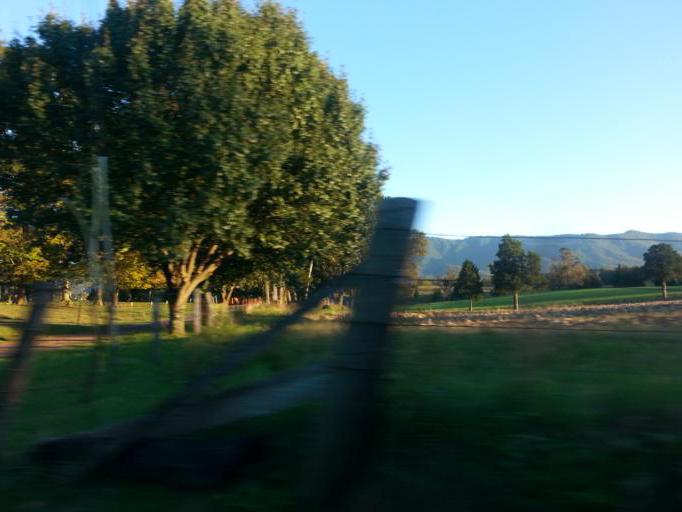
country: US
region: Tennessee
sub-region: Blount County
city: Wildwood
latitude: 35.8181
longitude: -83.7872
